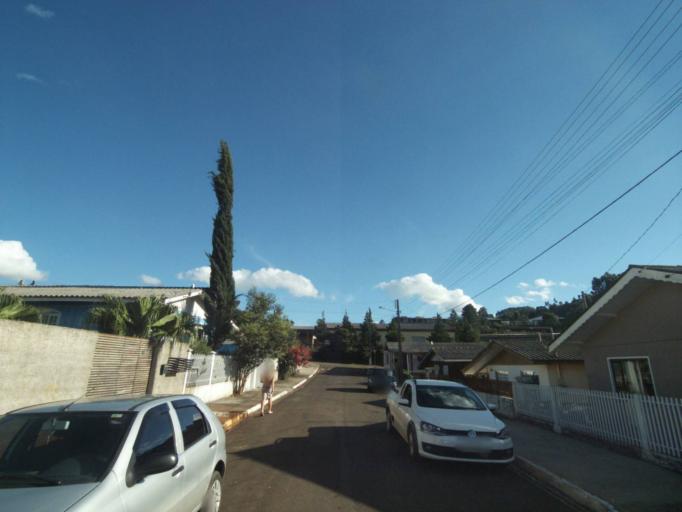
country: BR
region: Parana
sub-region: Uniao Da Vitoria
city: Uniao da Vitoria
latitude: -26.1603
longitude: -51.5380
